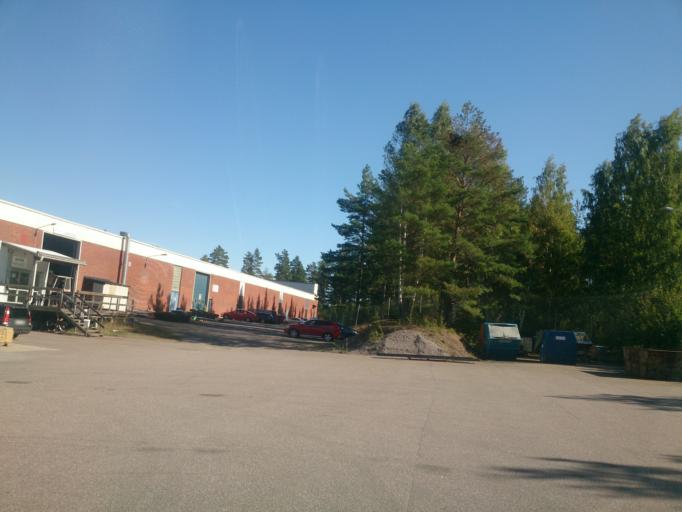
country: SE
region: OEstergoetland
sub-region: Atvidabergs Kommun
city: Atvidaberg
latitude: 58.2265
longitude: 15.9743
